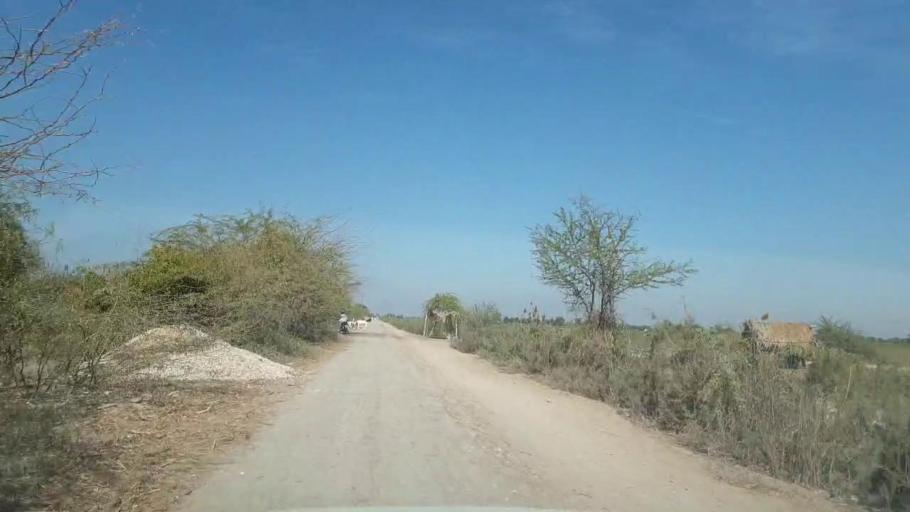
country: PK
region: Sindh
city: Pithoro
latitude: 25.6102
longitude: 69.2166
